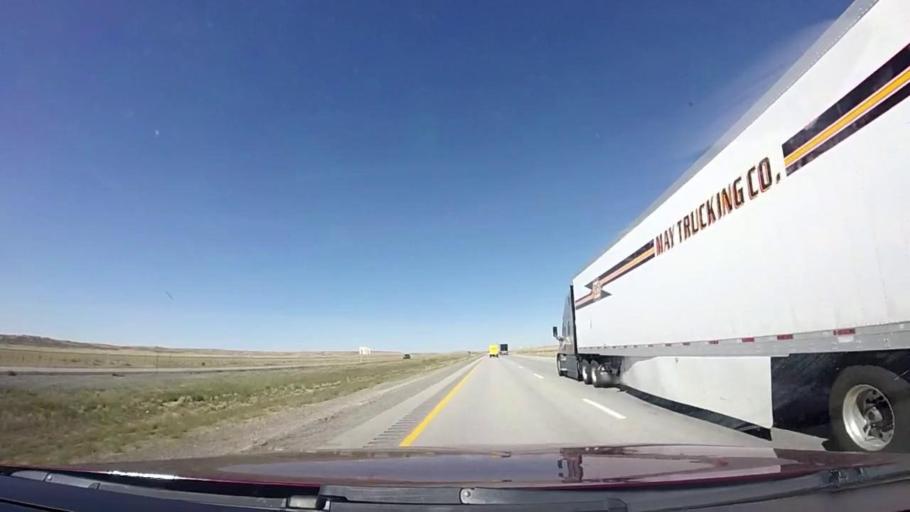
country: US
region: Wyoming
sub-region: Carbon County
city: Rawlins
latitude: 41.6642
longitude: -108.0407
